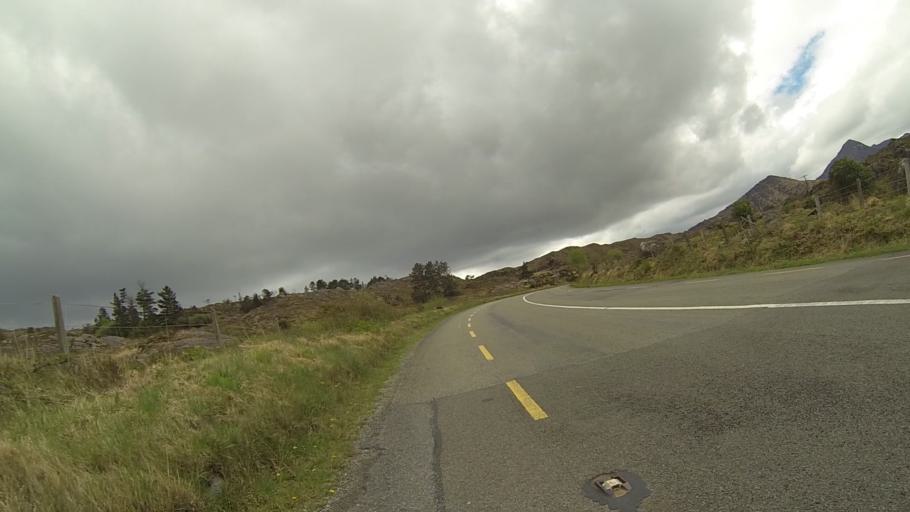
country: IE
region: Munster
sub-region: County Cork
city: Bantry
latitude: 51.7258
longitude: -9.5738
